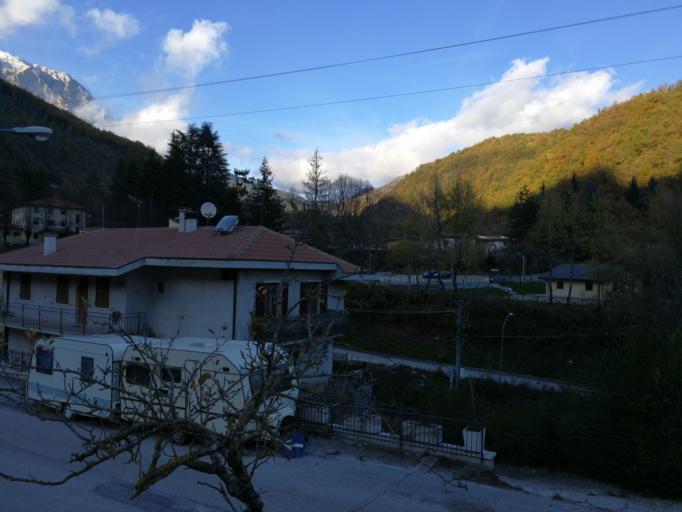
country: IT
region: The Marches
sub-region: Provincia di Ascoli Piceno
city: Arquata del Tronto
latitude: 42.7755
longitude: 13.2938
